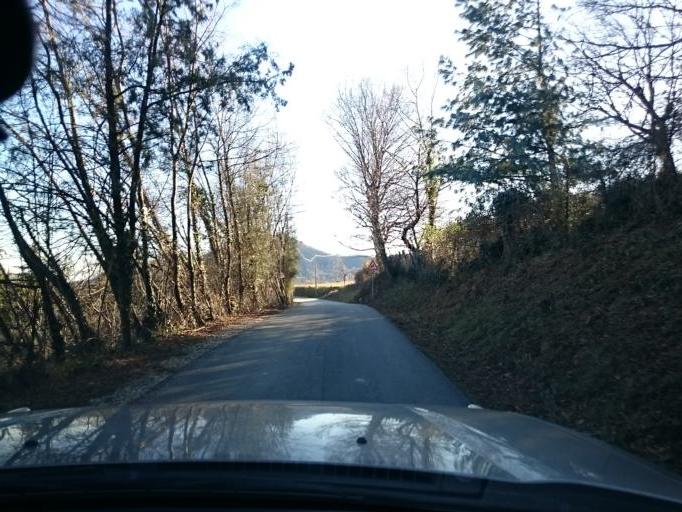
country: IT
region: Veneto
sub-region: Provincia di Padova
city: Treponti
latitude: 45.3360
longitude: 11.7033
